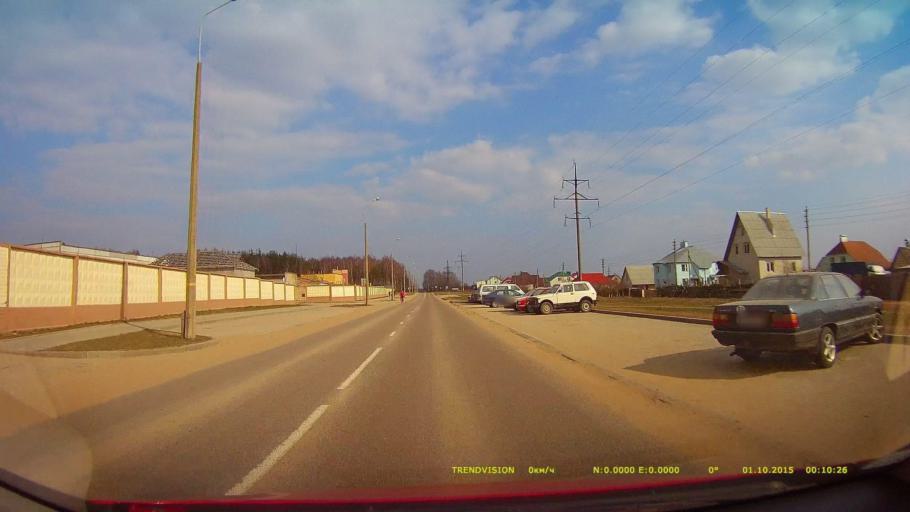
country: BY
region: Grodnenskaya
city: Lida
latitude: 53.9361
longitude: 25.2705
